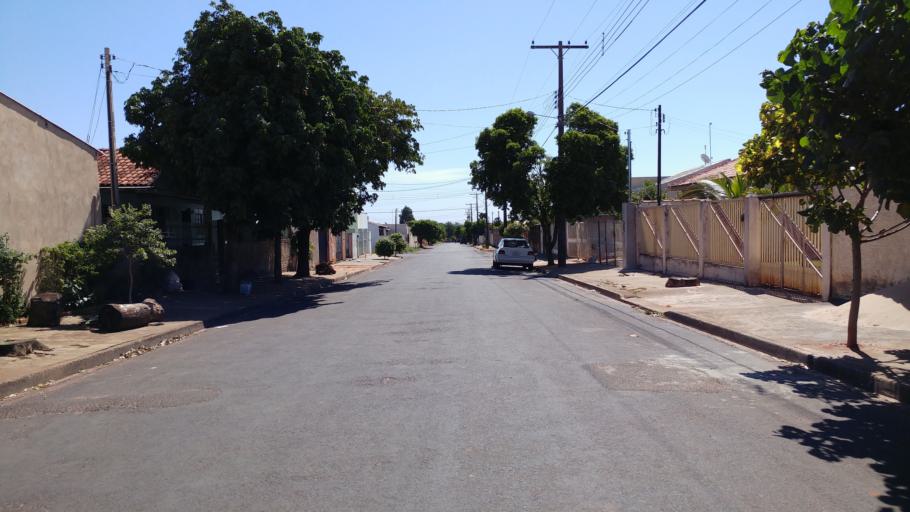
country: BR
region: Sao Paulo
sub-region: Paraguacu Paulista
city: Paraguacu Paulista
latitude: -22.4131
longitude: -50.5914
